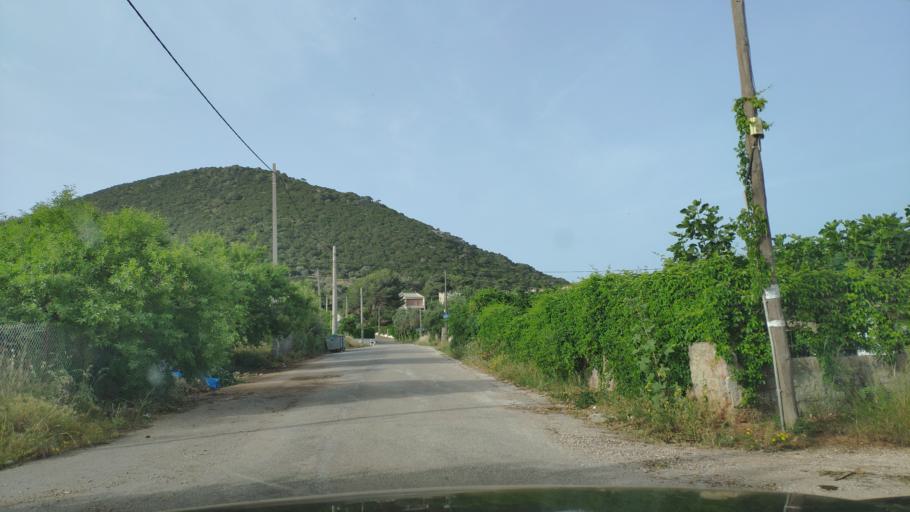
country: GR
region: Attica
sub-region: Nomarchia Anatolikis Attikis
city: Limin Mesoyaias
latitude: 37.8628
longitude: 24.0293
